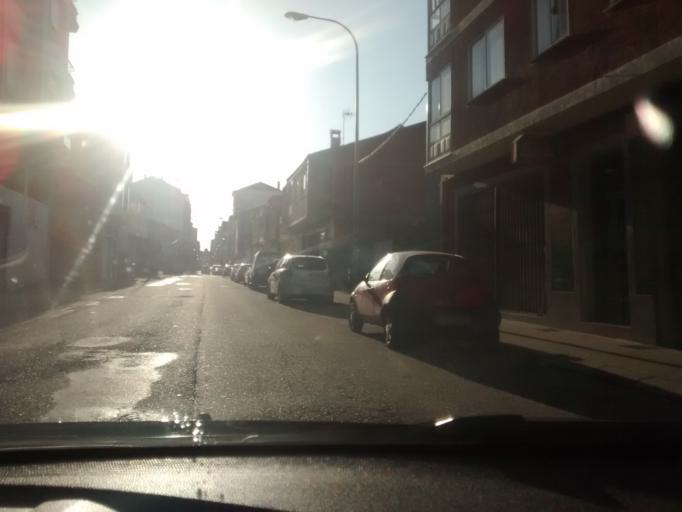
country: ES
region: Galicia
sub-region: Provincia de Pontevedra
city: A Estrada
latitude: 42.6900
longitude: -8.4812
